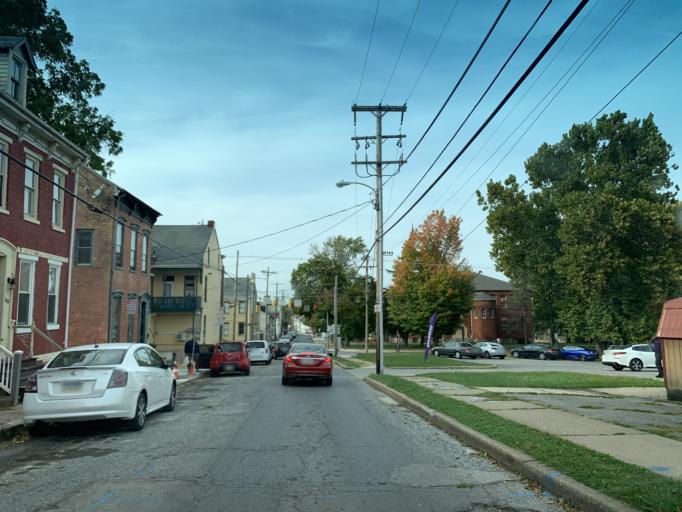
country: US
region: Pennsylvania
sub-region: York County
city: York
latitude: 39.9651
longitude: -76.7222
